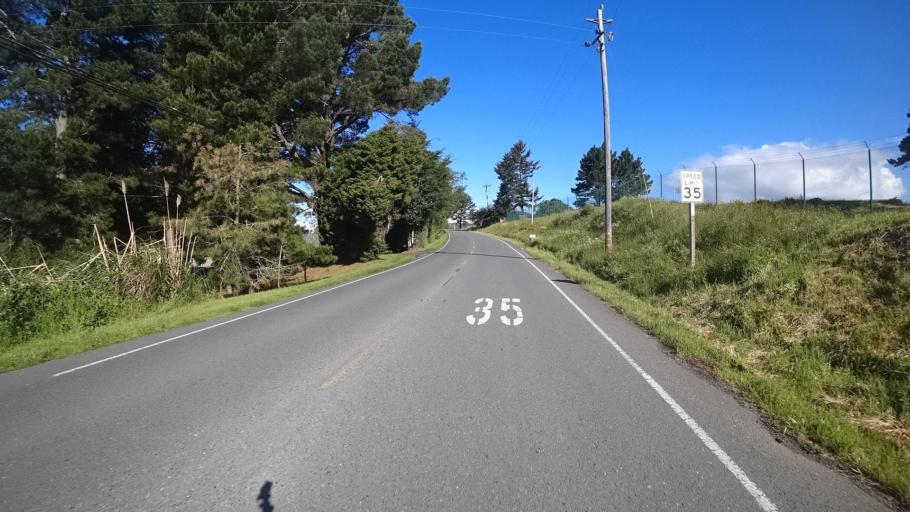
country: US
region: California
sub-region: Humboldt County
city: McKinleyville
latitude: 40.9641
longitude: -124.1011
